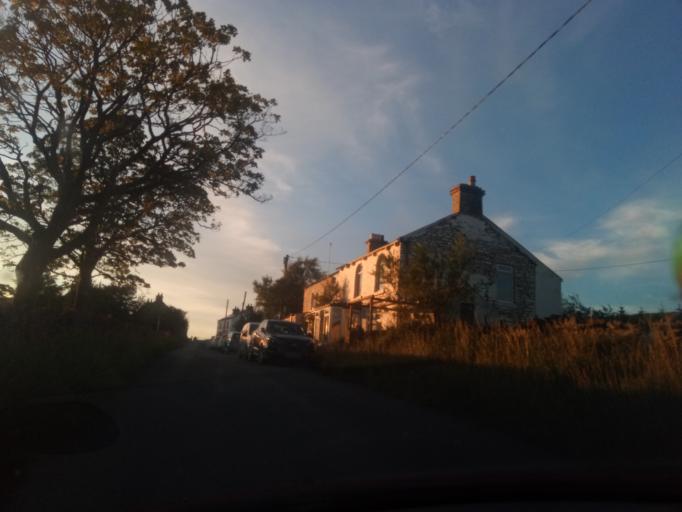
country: GB
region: England
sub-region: Northumberland
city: Bardon Mill
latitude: 54.7894
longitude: -2.3396
